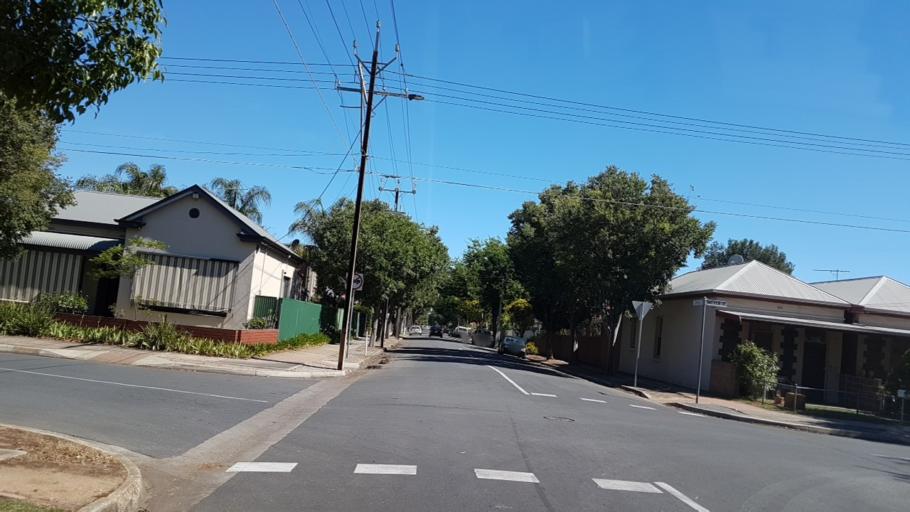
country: AU
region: South Australia
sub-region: City of West Torrens
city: Thebarton
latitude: -34.9163
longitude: 138.5607
